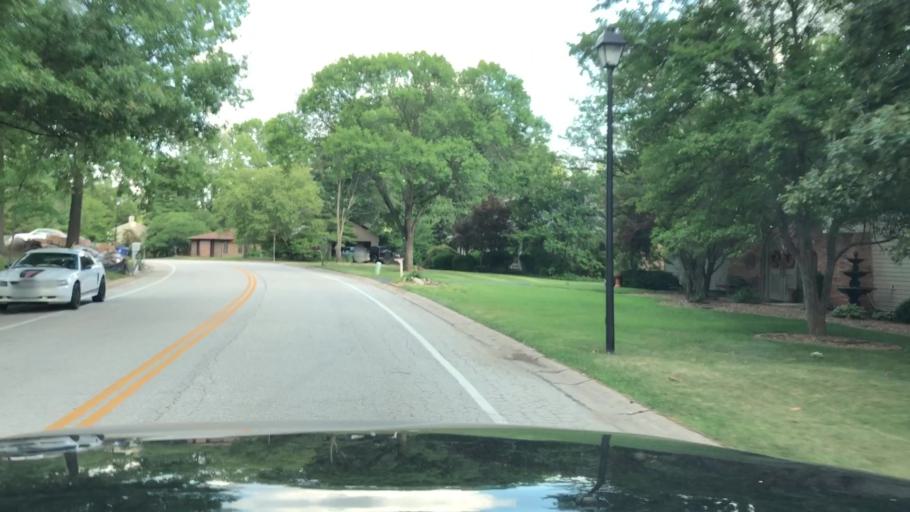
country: US
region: Missouri
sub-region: Saint Charles County
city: Lake Saint Louis
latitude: 38.7936
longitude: -90.7985
